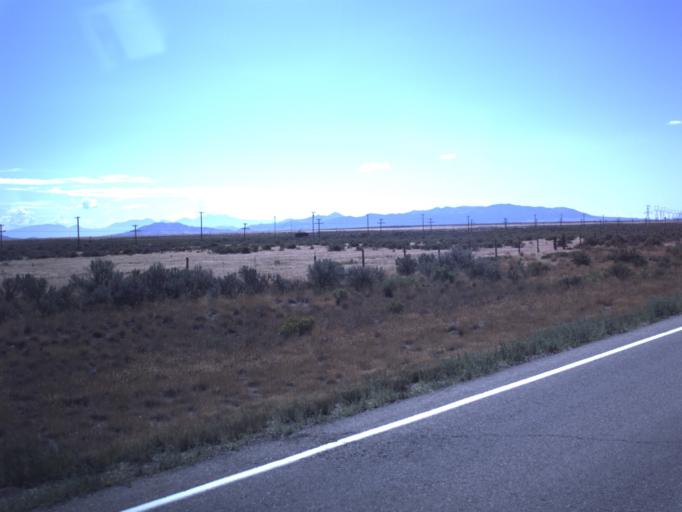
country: US
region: Utah
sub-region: Tooele County
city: Tooele
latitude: 40.2686
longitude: -112.3974
